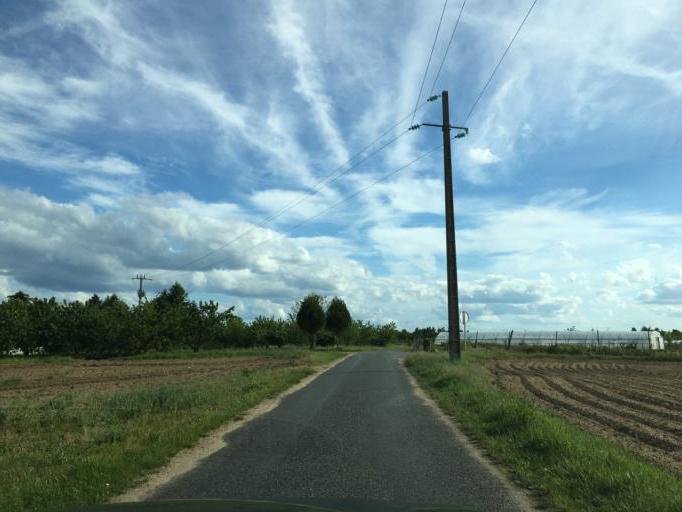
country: FR
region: Centre
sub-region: Departement du Loiret
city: Mareau-aux-Pres
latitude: 47.8412
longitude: 1.8072
